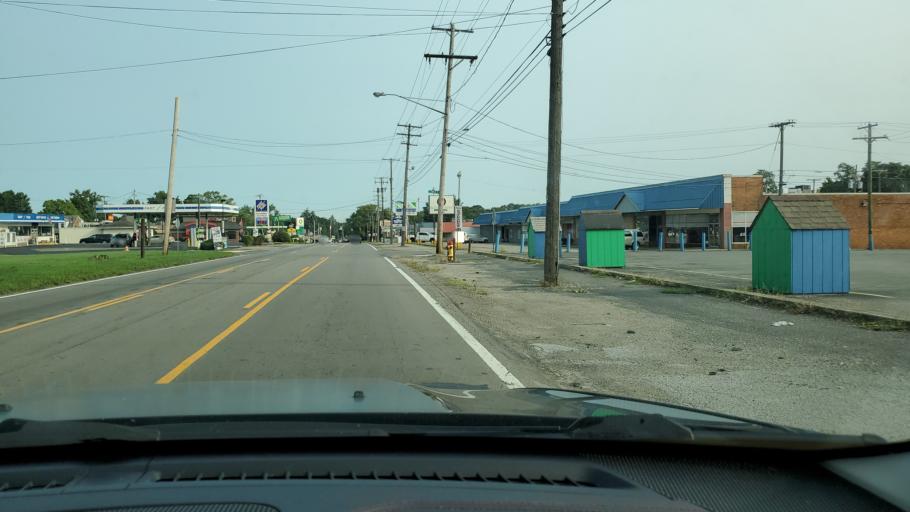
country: US
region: Ohio
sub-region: Mahoning County
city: Struthers
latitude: 41.0579
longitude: -80.6158
